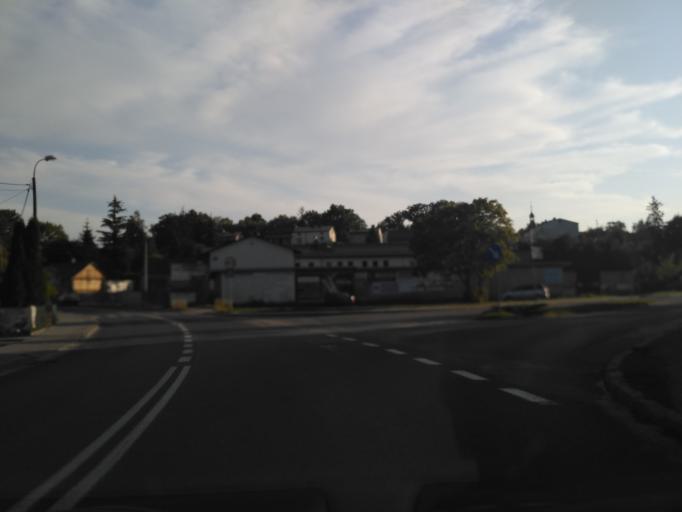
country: PL
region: Lublin Voivodeship
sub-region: Powiat lubelski
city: Bychawa
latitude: 51.0185
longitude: 22.5330
